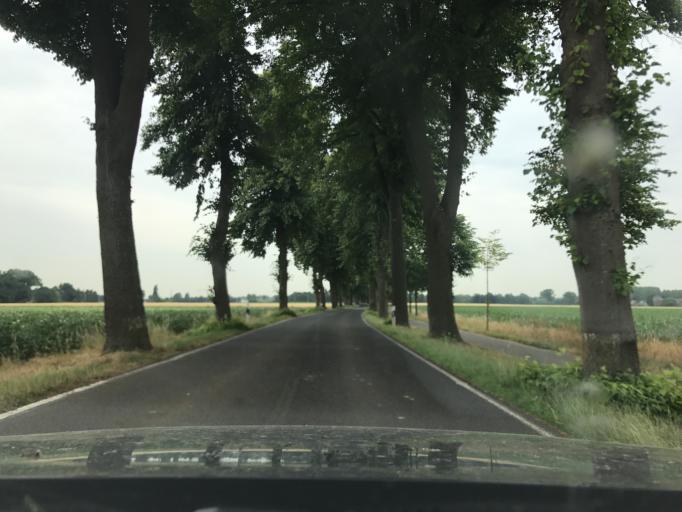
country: DE
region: North Rhine-Westphalia
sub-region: Regierungsbezirk Dusseldorf
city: Grefrath
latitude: 51.3567
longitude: 6.3650
